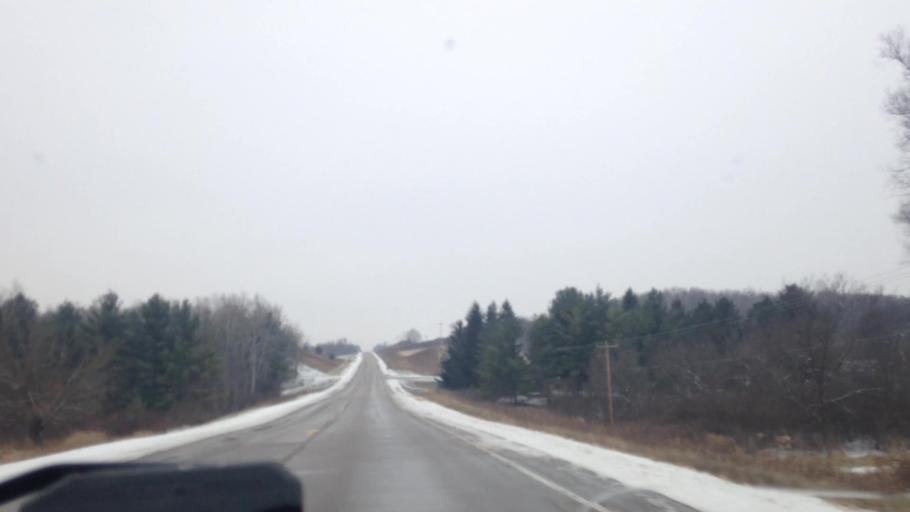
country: US
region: Wisconsin
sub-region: Dodge County
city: Hustisford
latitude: 43.2811
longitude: -88.5185
